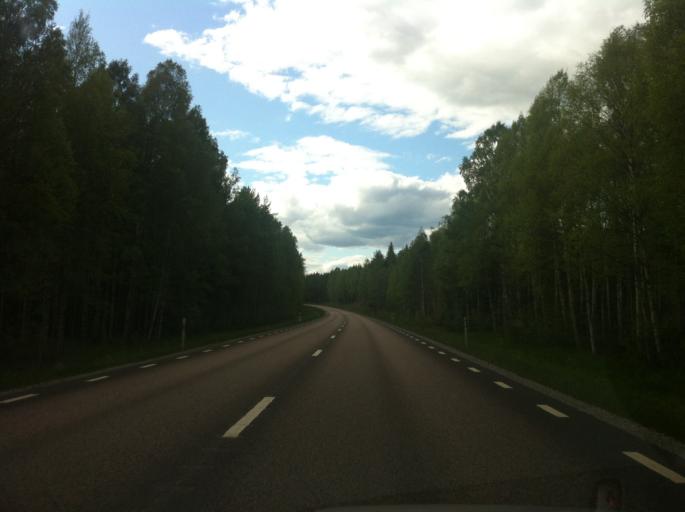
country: SE
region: Vaermland
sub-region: Filipstads Kommun
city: Filipstad
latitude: 59.6430
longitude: 14.2523
